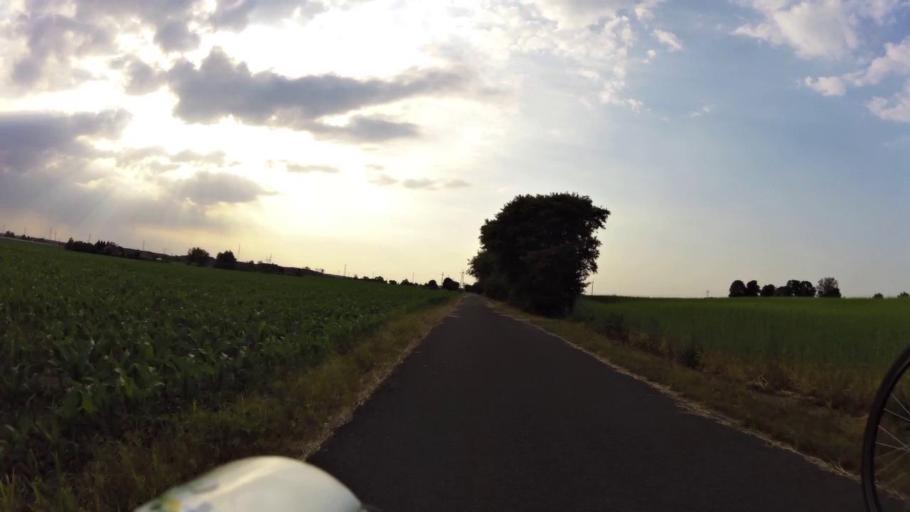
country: PL
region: Kujawsko-Pomorskie
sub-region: Powiat chelminski
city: Unislaw
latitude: 53.1774
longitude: 18.4117
